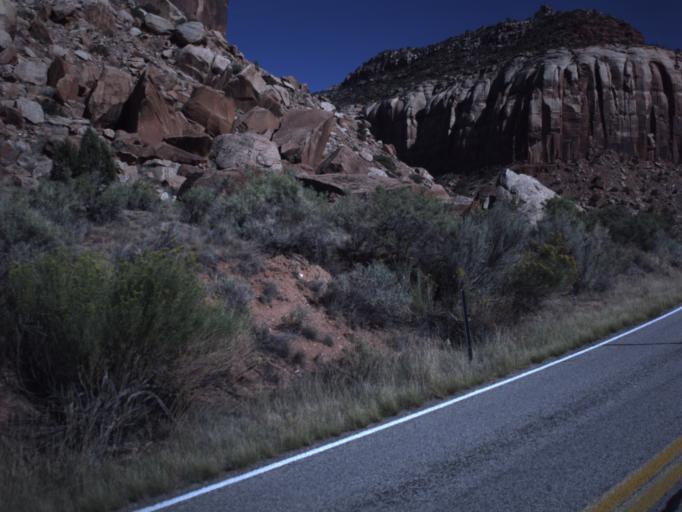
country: US
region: Utah
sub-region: San Juan County
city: Monticello
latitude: 38.0385
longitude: -109.5521
